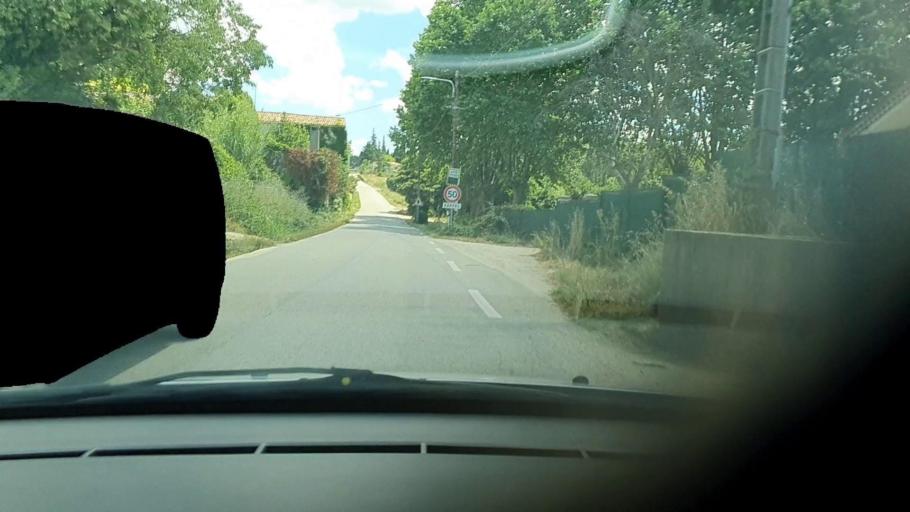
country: FR
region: Languedoc-Roussillon
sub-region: Departement du Gard
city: Moussac
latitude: 44.0551
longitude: 4.2241
